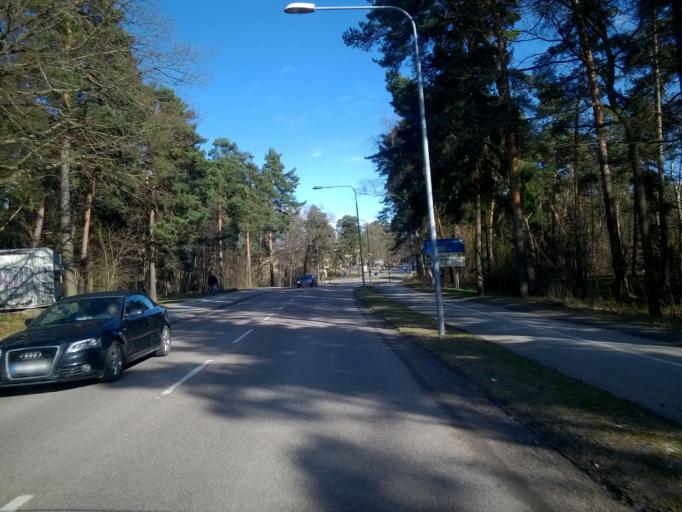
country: SE
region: Stockholm
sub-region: Stockholms Kommun
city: Bromma
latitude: 59.3289
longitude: 17.9535
